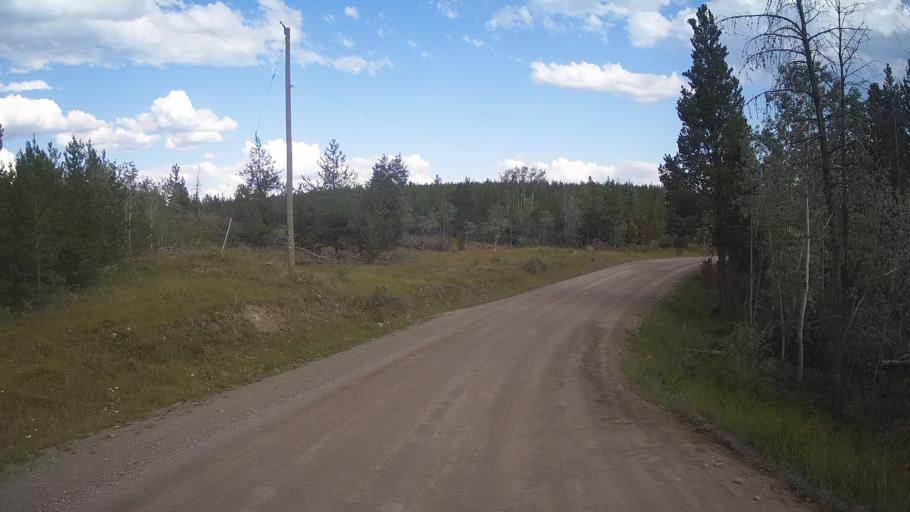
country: CA
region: British Columbia
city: Lillooet
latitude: 51.2872
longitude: -121.7497
